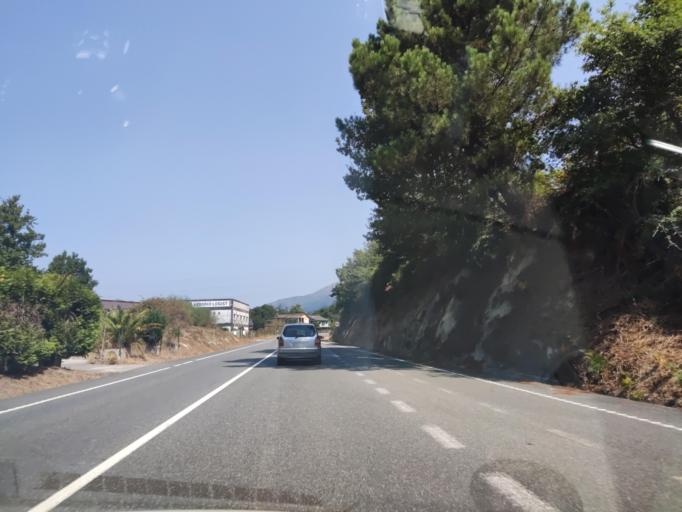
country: ES
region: Galicia
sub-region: Provincia de Pontevedra
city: Porrino
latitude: 42.1918
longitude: -8.6083
